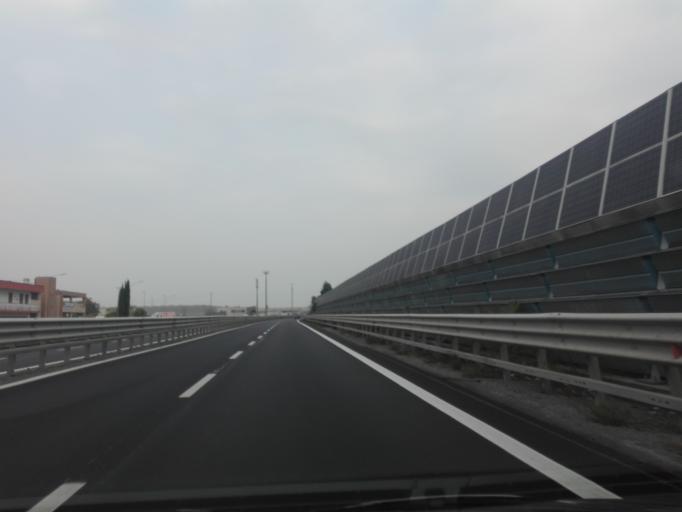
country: IT
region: Veneto
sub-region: Provincia di Verona
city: Vallese
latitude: 45.3270
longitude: 11.0822
